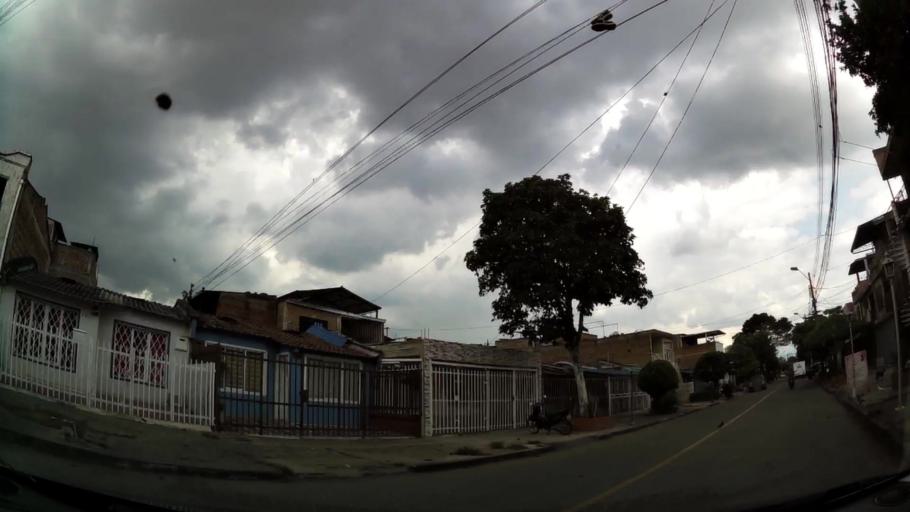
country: CO
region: Valle del Cauca
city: Cali
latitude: 3.4592
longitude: -76.4873
